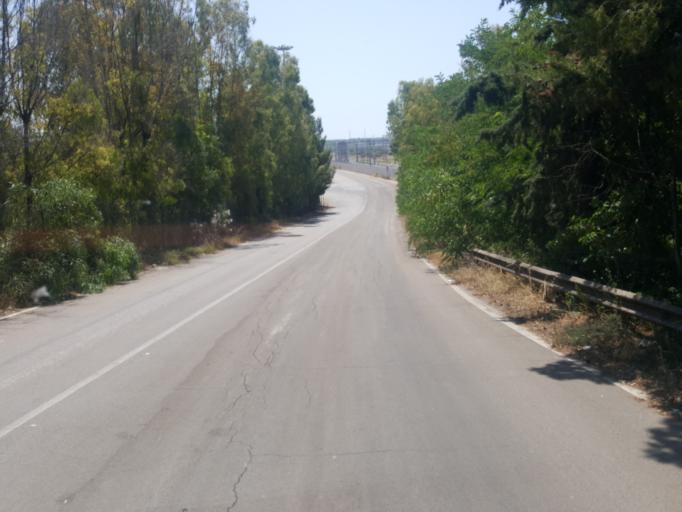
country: IT
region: Apulia
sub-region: Provincia di Taranto
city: Statte
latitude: 40.5130
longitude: 17.1833
